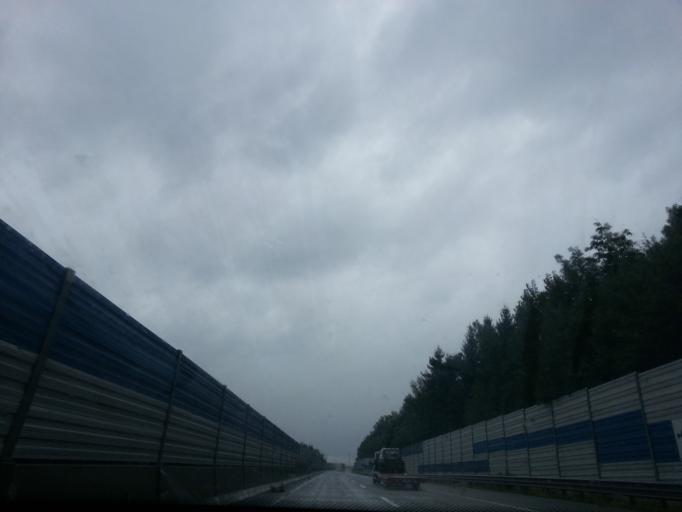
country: AT
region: Upper Austria
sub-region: Politischer Bezirk Vocklabruck
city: Oberwang
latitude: 47.8742
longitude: 13.4350
